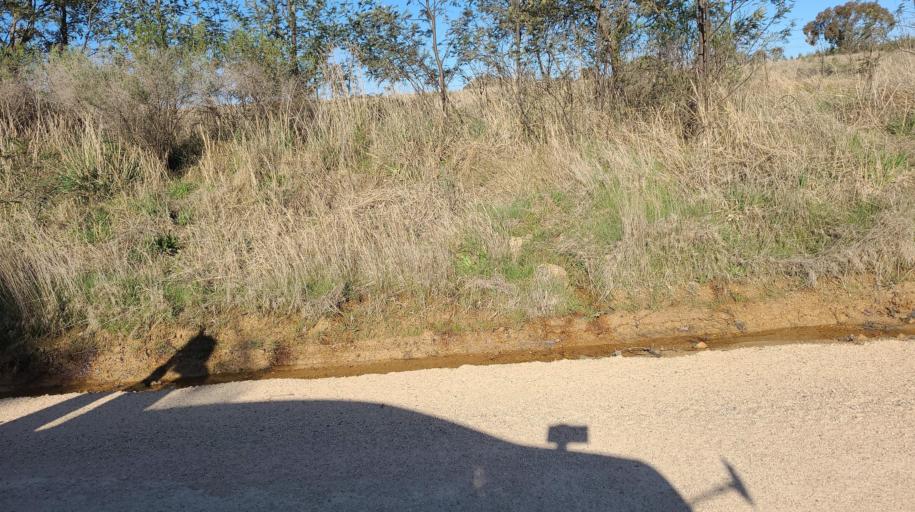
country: AU
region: New South Wales
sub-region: Blayney
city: Millthorpe
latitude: -33.3957
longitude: 149.3094
